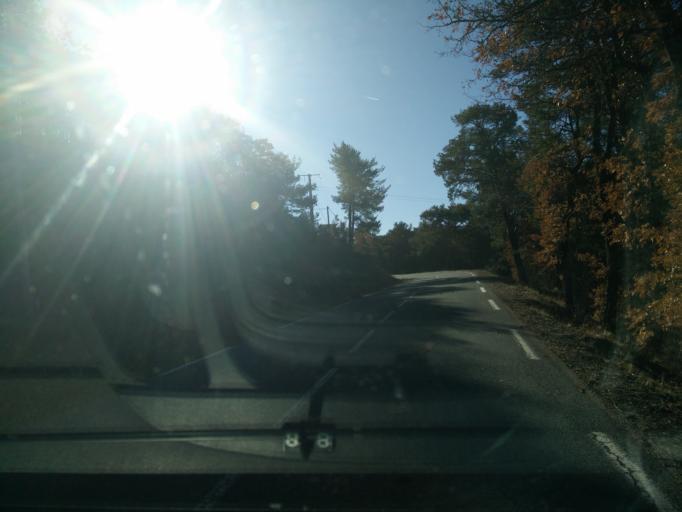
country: FR
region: Provence-Alpes-Cote d'Azur
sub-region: Departement des Alpes-de-Haute-Provence
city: Castellane
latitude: 43.7945
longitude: 6.4429
